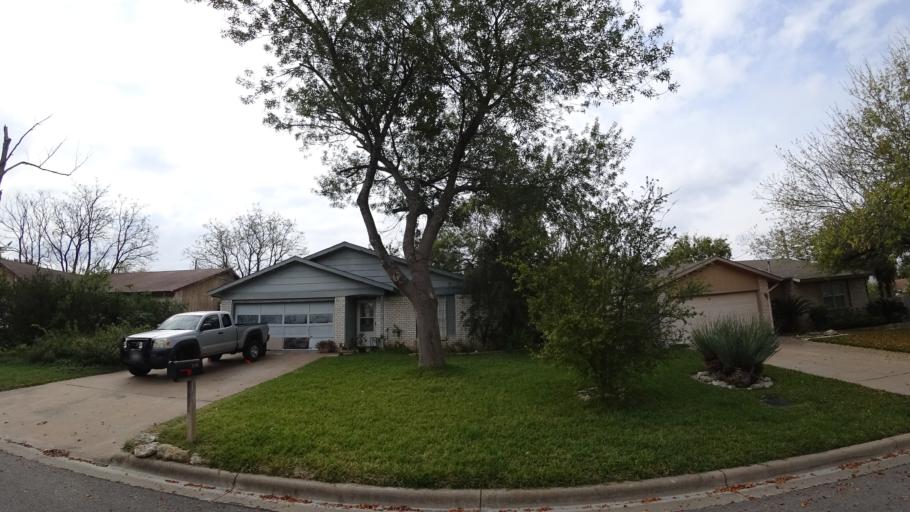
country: US
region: Texas
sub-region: Williamson County
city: Round Rock
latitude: 30.4902
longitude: -97.6871
